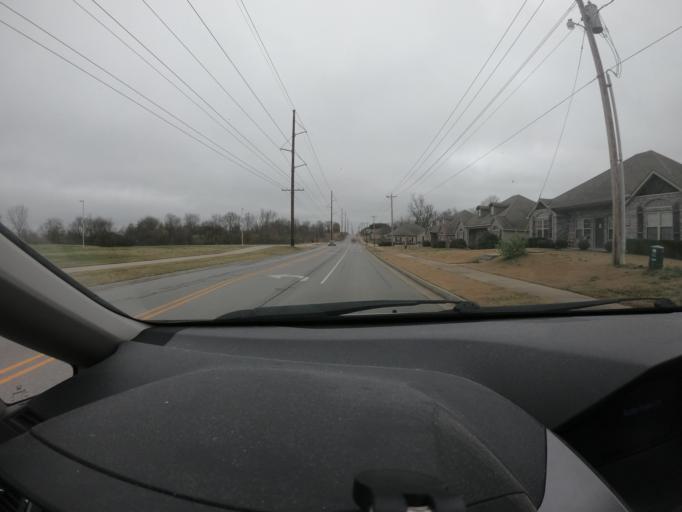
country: US
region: Arkansas
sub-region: Benton County
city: Centerton
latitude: 36.3412
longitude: -94.2451
